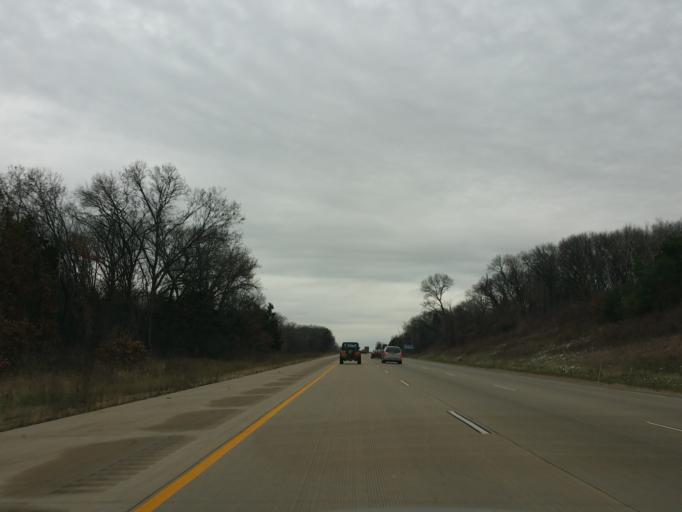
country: US
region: Wisconsin
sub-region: Columbia County
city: Poynette
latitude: 43.3853
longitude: -89.4656
